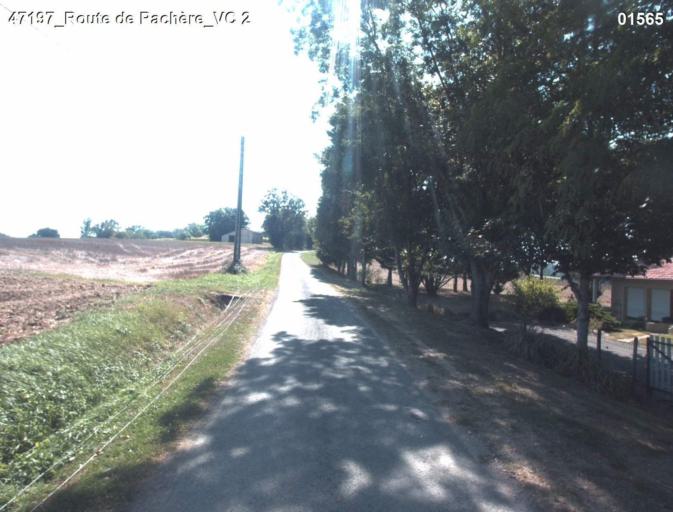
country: FR
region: Aquitaine
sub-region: Departement du Lot-et-Garonne
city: Laplume
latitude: 44.0899
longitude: 0.4550
